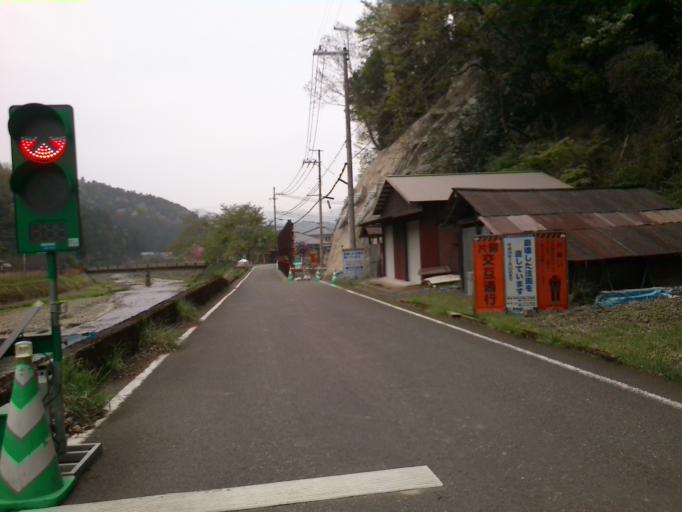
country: JP
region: Kyoto
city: Maizuru
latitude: 35.3678
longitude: 135.4561
